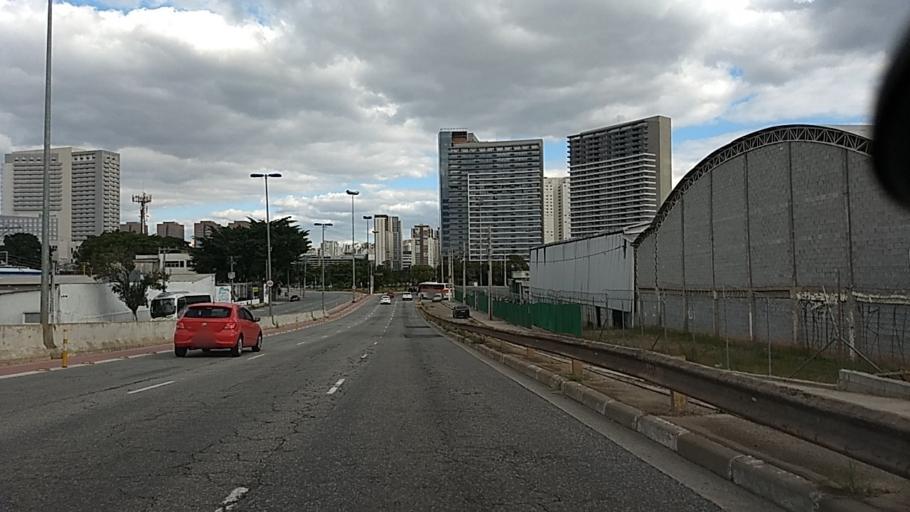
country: BR
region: Sao Paulo
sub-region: Sao Paulo
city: Sao Paulo
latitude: -23.5154
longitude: -46.6791
